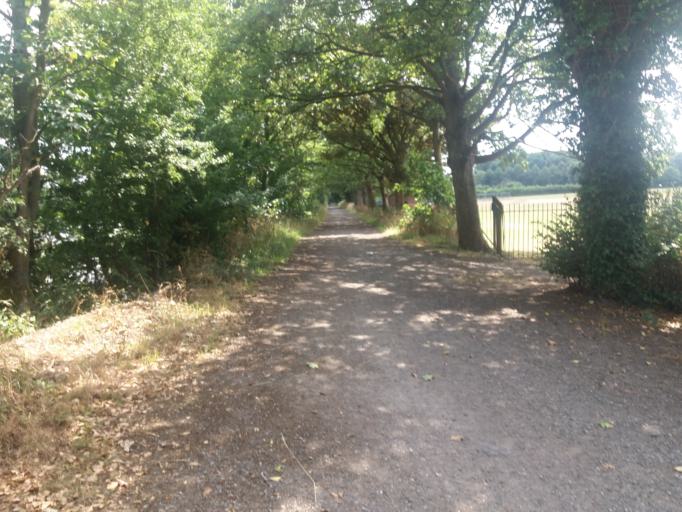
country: GB
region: England
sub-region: Lancashire
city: Preston
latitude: 53.7532
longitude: -2.7184
